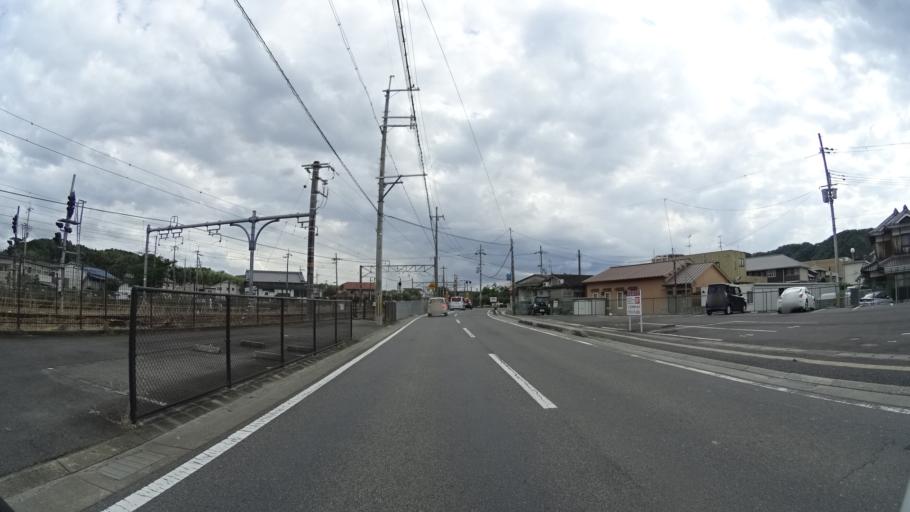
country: JP
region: Nara
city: Nara-shi
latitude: 34.7517
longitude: 135.8685
